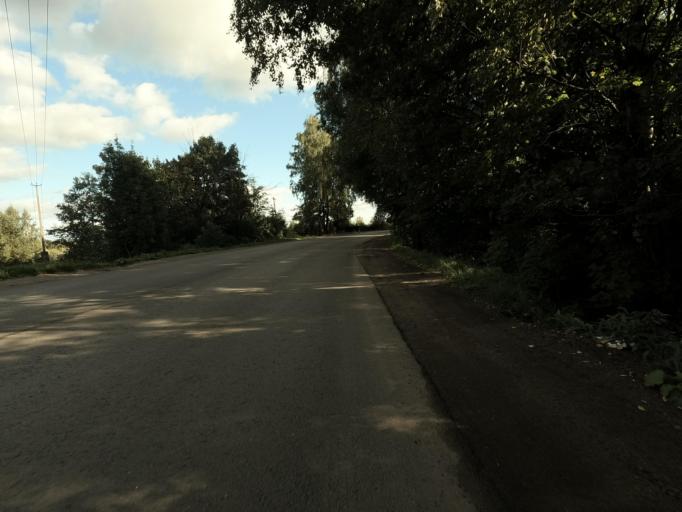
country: RU
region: Leningrad
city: Koltushi
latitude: 59.9362
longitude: 30.6641
